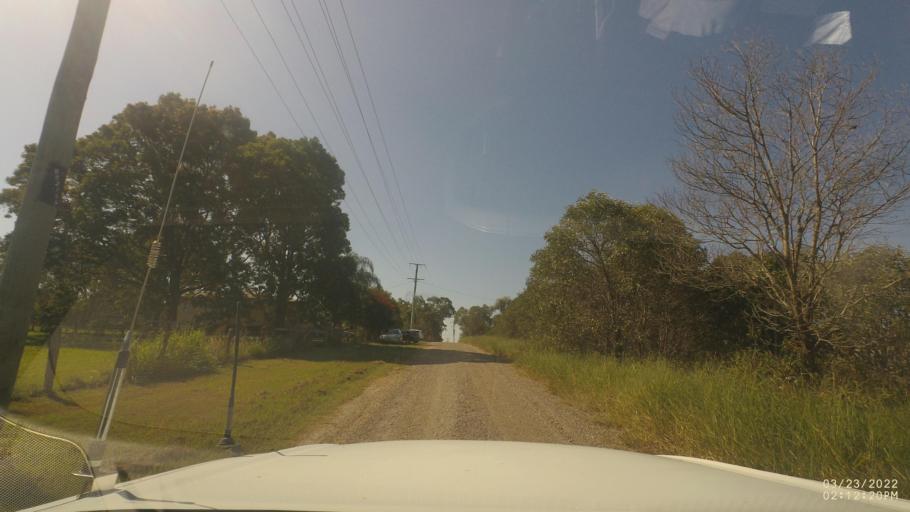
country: AU
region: Queensland
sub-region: Logan
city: Logan Reserve
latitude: -27.7424
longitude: 153.1253
